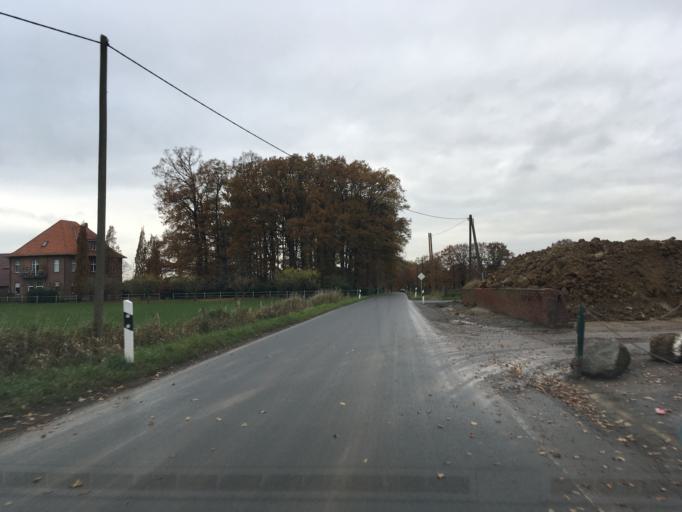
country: DE
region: North Rhine-Westphalia
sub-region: Regierungsbezirk Munster
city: Gescher
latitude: 51.9712
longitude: 7.0125
